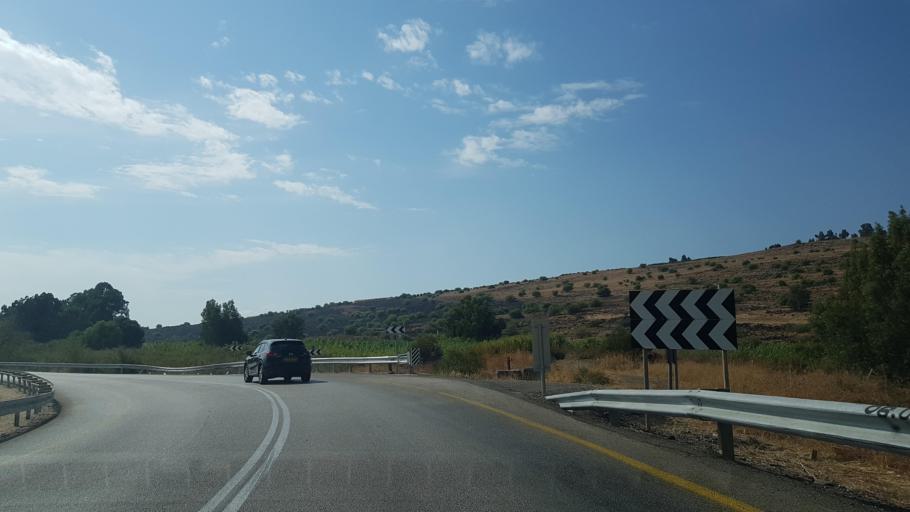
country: SY
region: Quneitra
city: Al Butayhah
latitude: 32.9045
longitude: 35.6184
